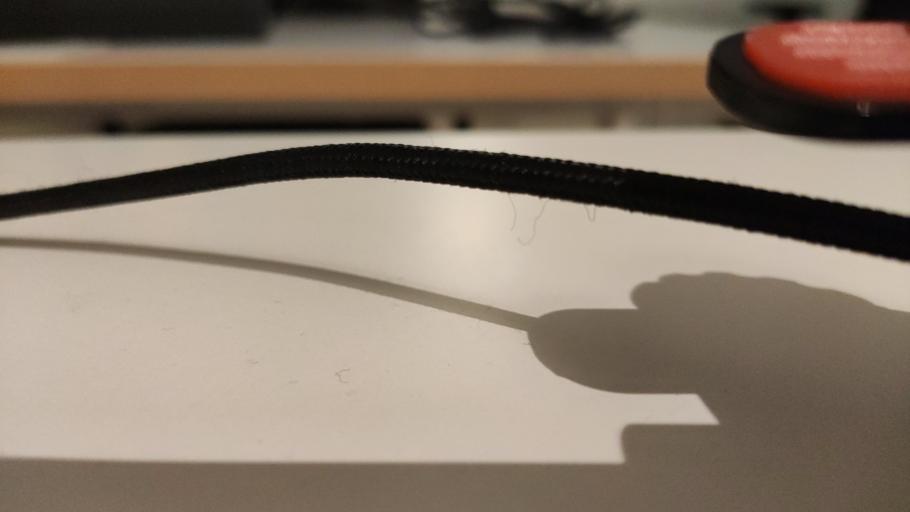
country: RU
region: Moskovskaya
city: Novosin'kovo
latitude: 56.3922
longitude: 37.2894
